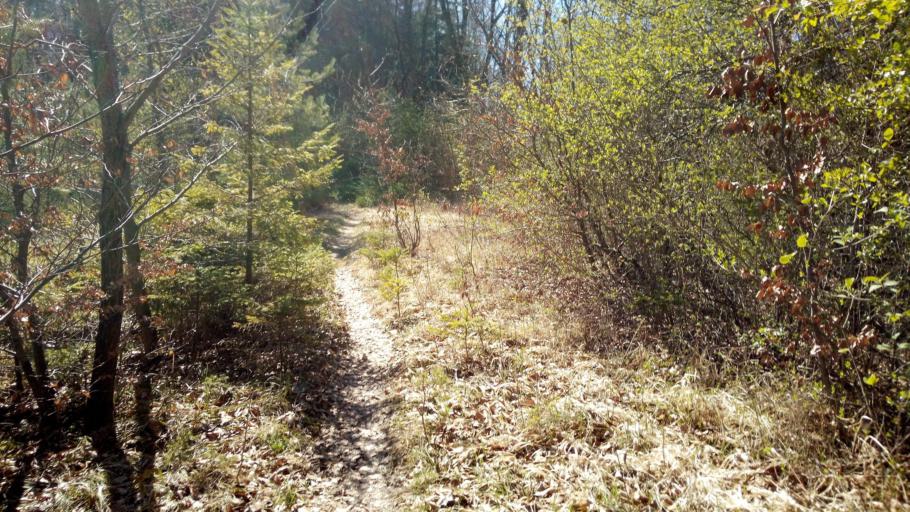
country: DE
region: Baden-Wuerttemberg
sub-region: Regierungsbezirk Stuttgart
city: Donzdorf
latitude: 48.7116
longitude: 9.8433
